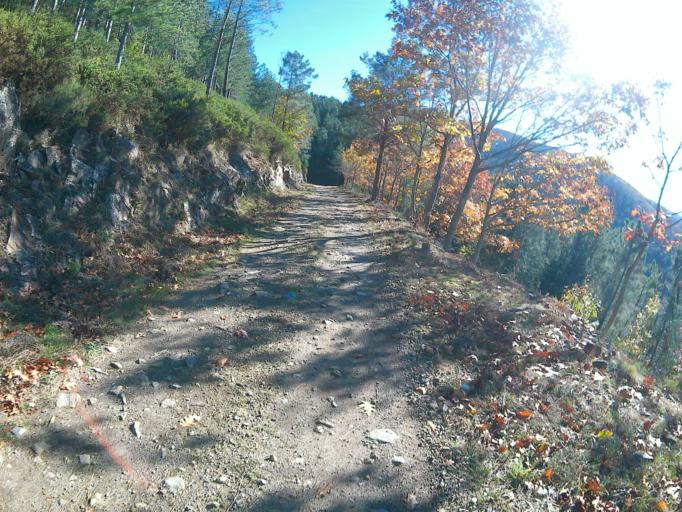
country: PT
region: Vila Real
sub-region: Mesao Frio
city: Mesao Frio
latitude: 41.2423
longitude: -7.9313
